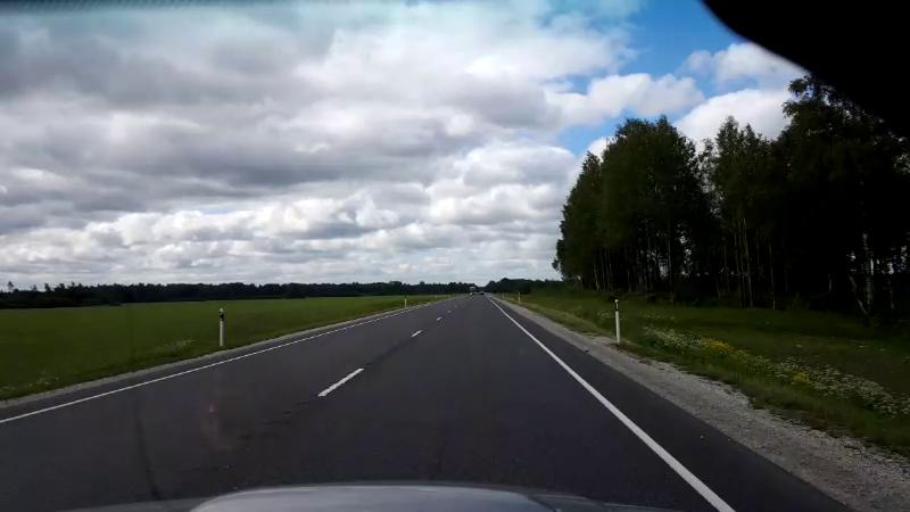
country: EE
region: Raplamaa
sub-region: Maerjamaa vald
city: Marjamaa
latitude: 58.8501
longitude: 24.4298
